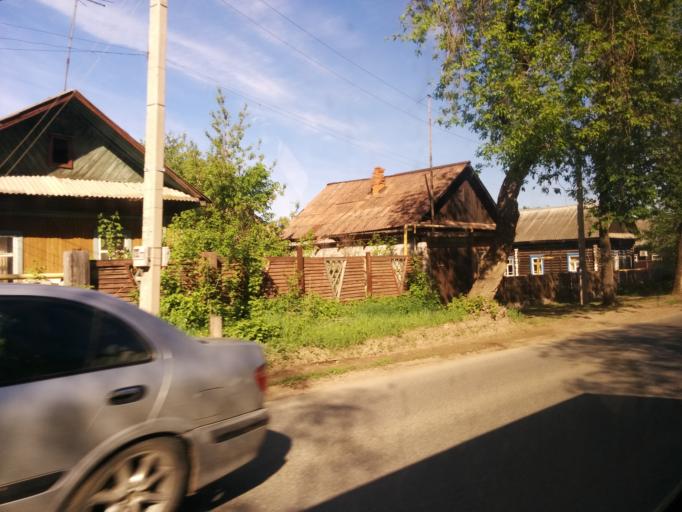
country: RU
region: Perm
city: Kondratovo
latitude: 58.0428
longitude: 56.1062
